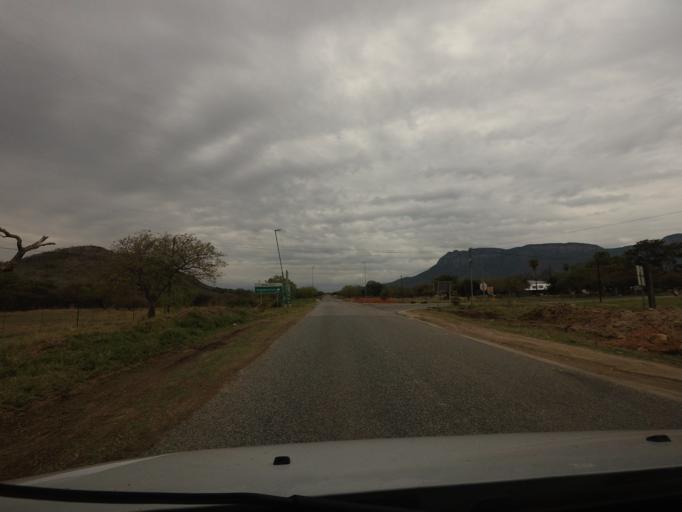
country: ZA
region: Limpopo
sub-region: Mopani District Municipality
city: Hoedspruit
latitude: -24.4995
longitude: 30.8948
